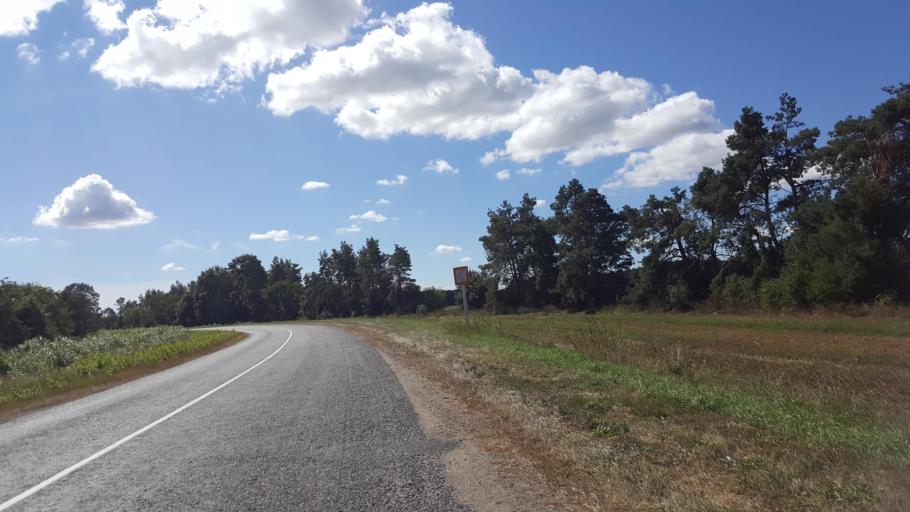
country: BY
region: Brest
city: Vysokaye
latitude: 52.3265
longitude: 23.3234
